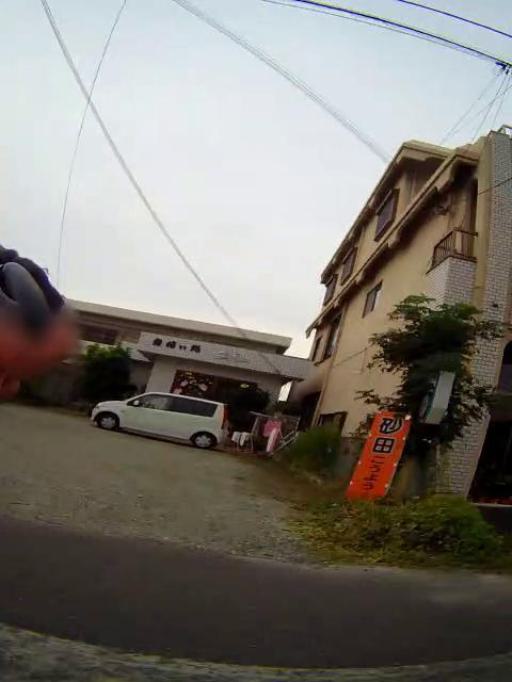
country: JP
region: Hyogo
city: Fukura
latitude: 34.2840
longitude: 134.7741
